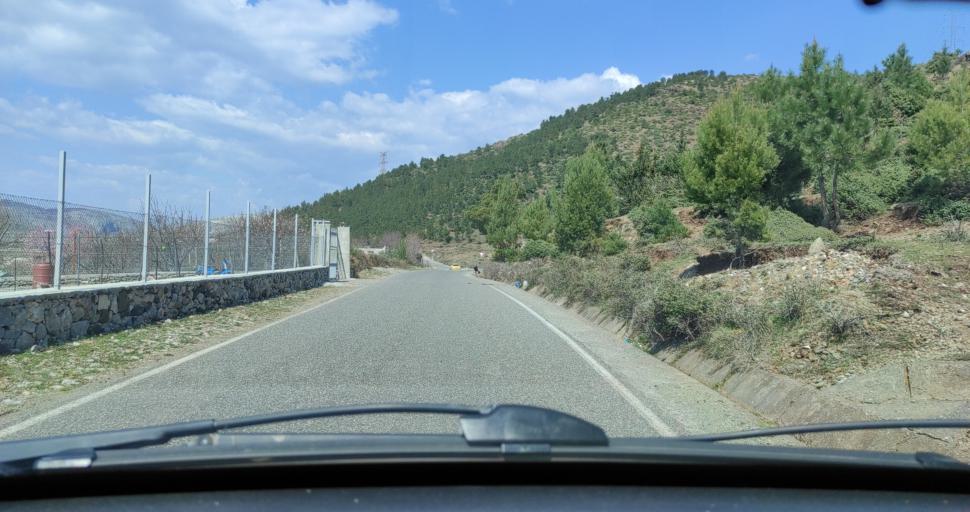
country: AL
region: Shkoder
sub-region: Rrethi i Shkodres
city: Vau i Dejes
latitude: 41.9982
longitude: 19.6496
